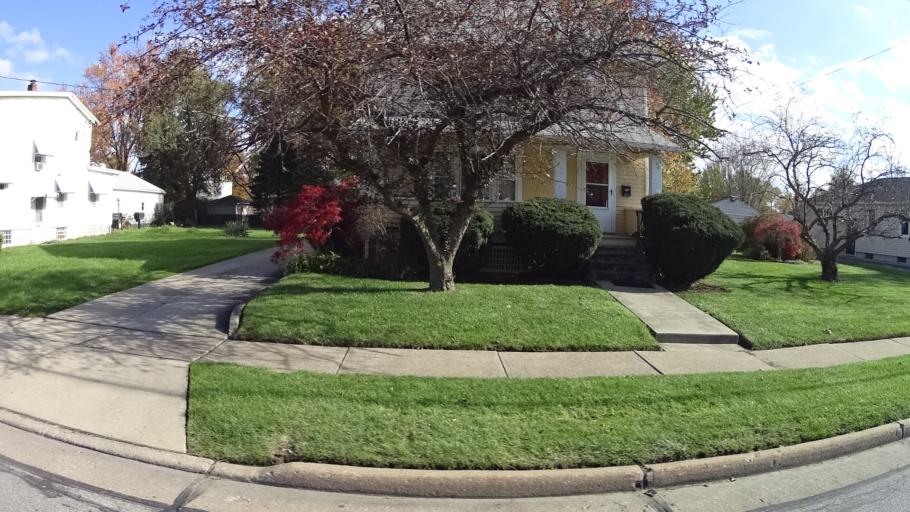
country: US
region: Ohio
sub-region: Lorain County
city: Lorain
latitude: 41.4580
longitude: -82.2023
